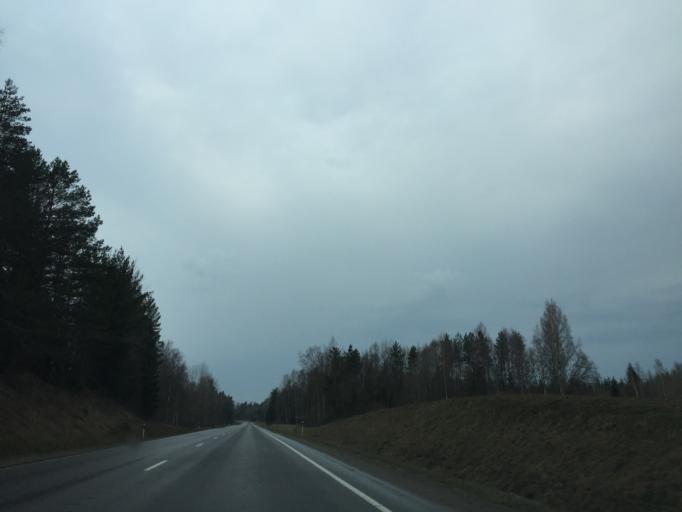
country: EE
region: Tartu
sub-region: UElenurme vald
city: Ulenurme
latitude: 58.1174
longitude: 26.7339
